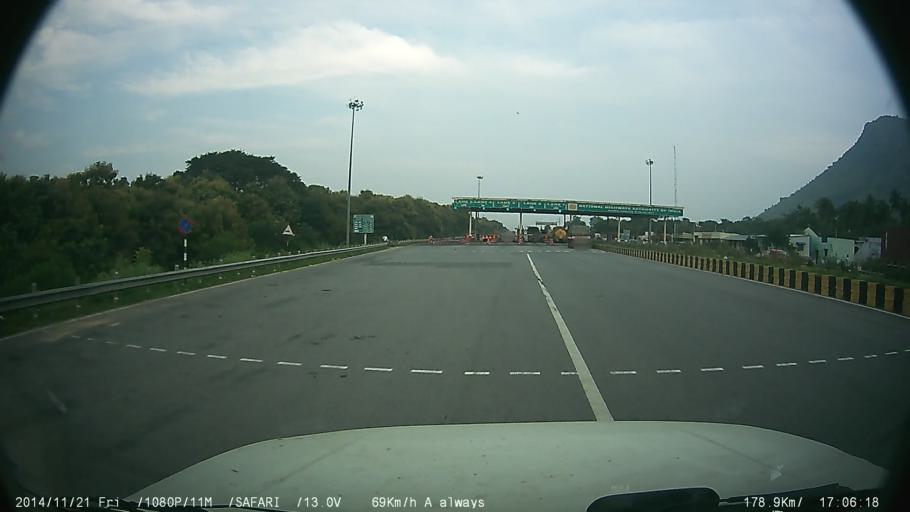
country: IN
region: Tamil Nadu
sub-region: Vellore
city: Pallikondai
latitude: 12.9057
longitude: 78.9504
